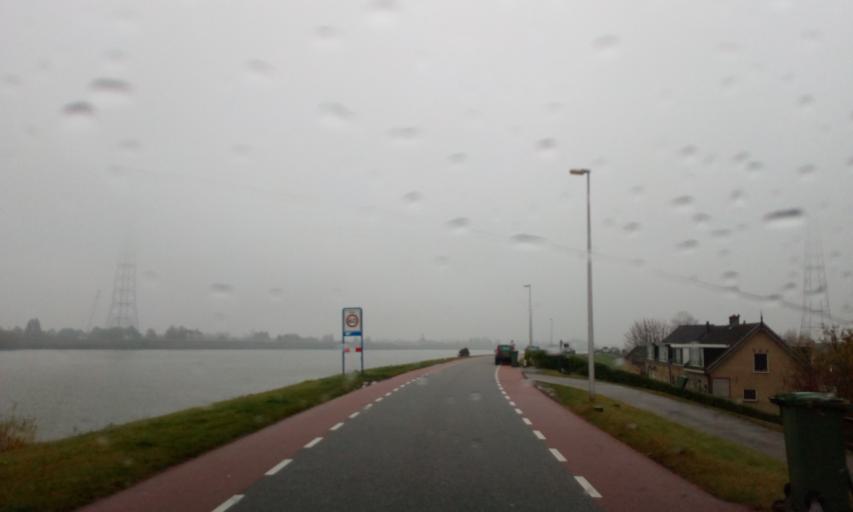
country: NL
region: South Holland
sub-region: Molenwaard
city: Nieuw-Lekkerland
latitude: 51.8921
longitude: 4.6743
